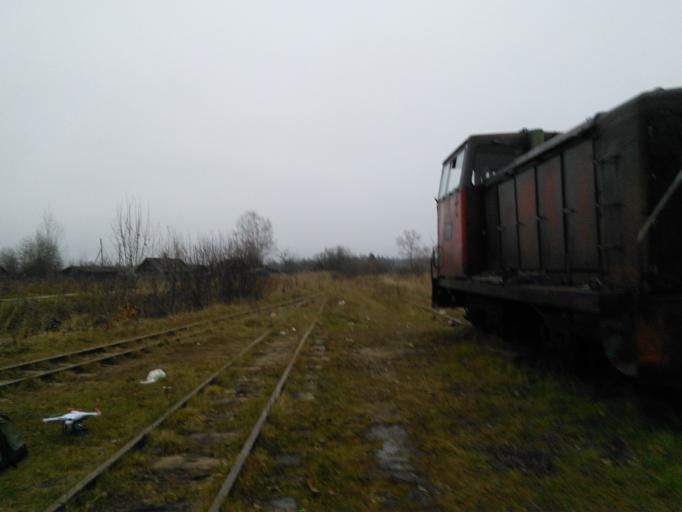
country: RU
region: Vologda
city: Kharovsk
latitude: 59.8075
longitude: 40.1763
